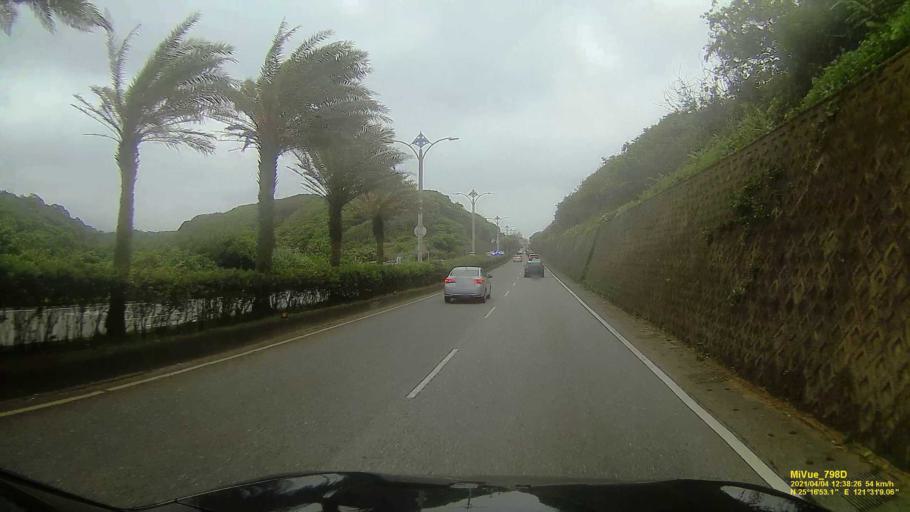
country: TW
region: Taipei
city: Taipei
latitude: 25.2811
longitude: 121.5191
